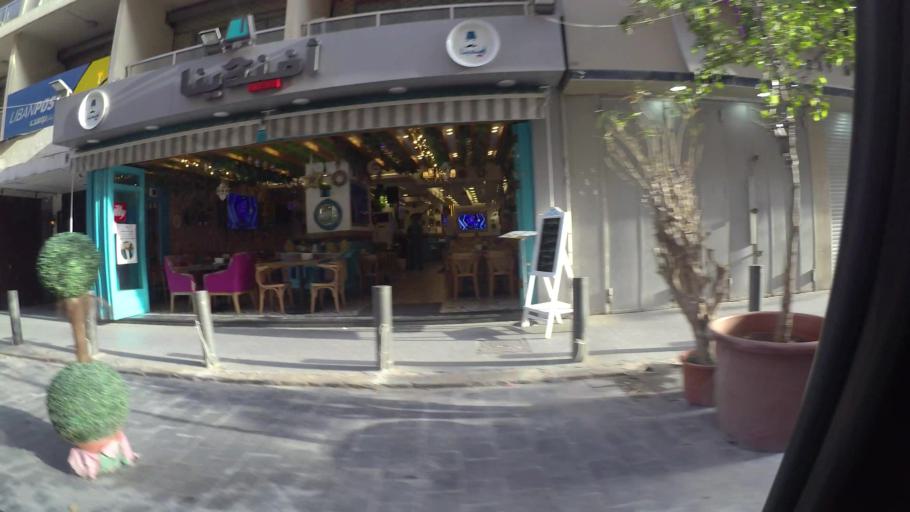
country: LB
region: Beyrouth
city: Ra's Bayrut
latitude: 33.8964
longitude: 35.4821
